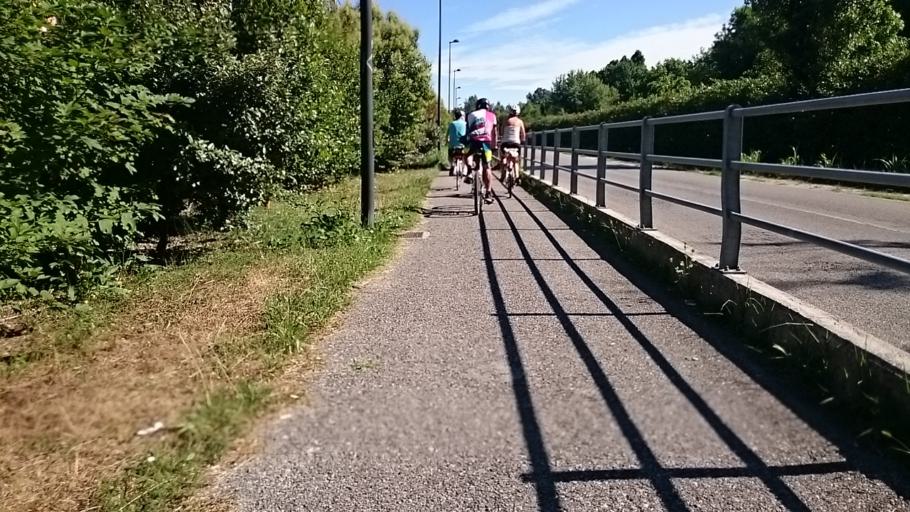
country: IT
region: Veneto
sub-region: Provincia di Padova
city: Camposampiero
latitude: 45.5750
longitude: 11.9311
